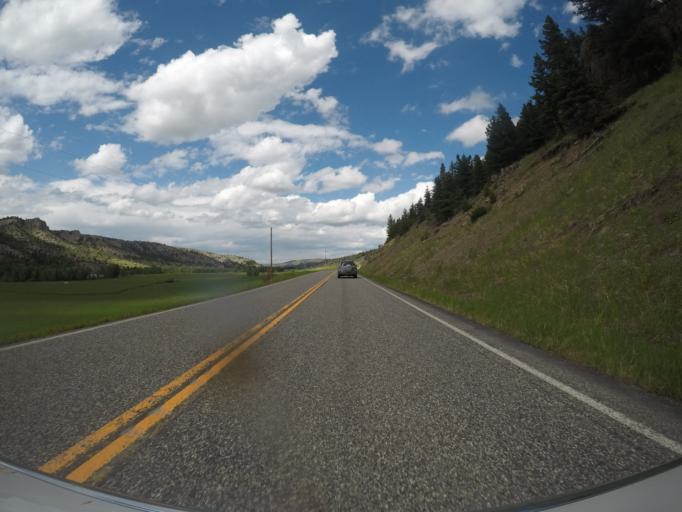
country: US
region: Montana
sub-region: Sweet Grass County
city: Big Timber
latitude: 45.7018
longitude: -110.0163
